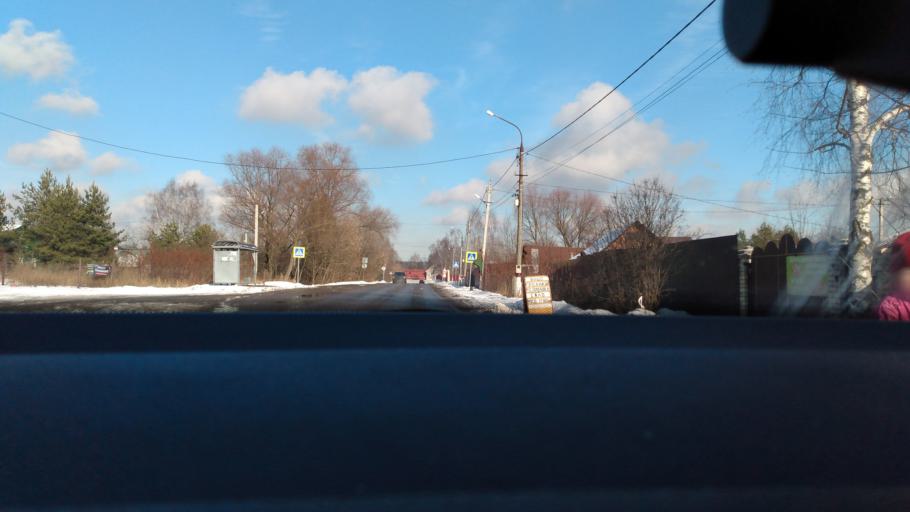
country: RU
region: Moskovskaya
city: Kratovo
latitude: 55.6364
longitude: 38.1647
